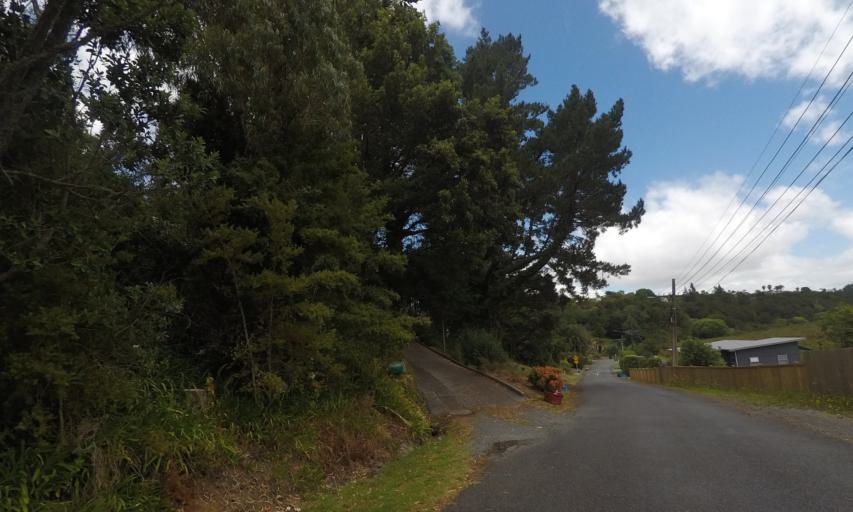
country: NZ
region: Northland
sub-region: Whangarei
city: Whangarei
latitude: -35.7436
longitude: 174.3605
